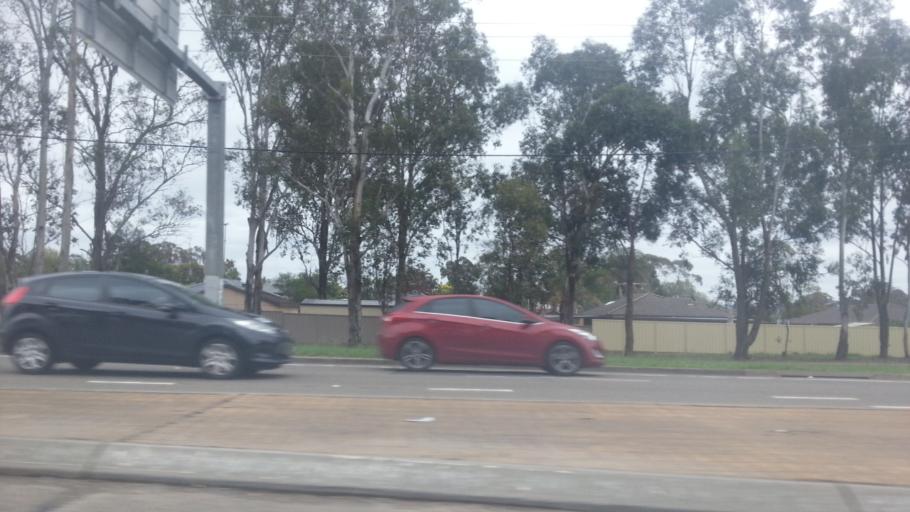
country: AU
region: New South Wales
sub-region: Penrith Municipality
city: Werrington Downs
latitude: -33.7368
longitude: 150.7173
